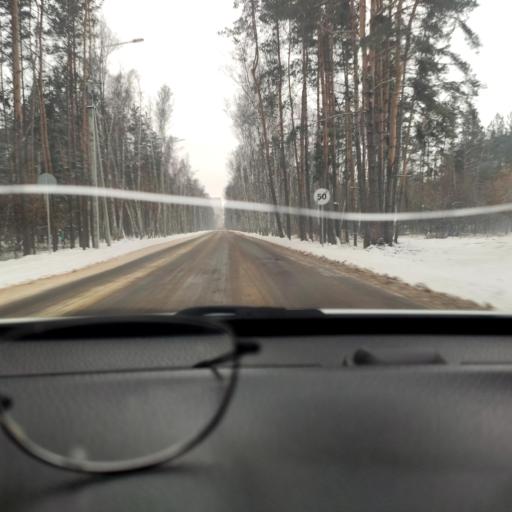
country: RU
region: Voronezj
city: Somovo
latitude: 51.7004
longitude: 39.2823
